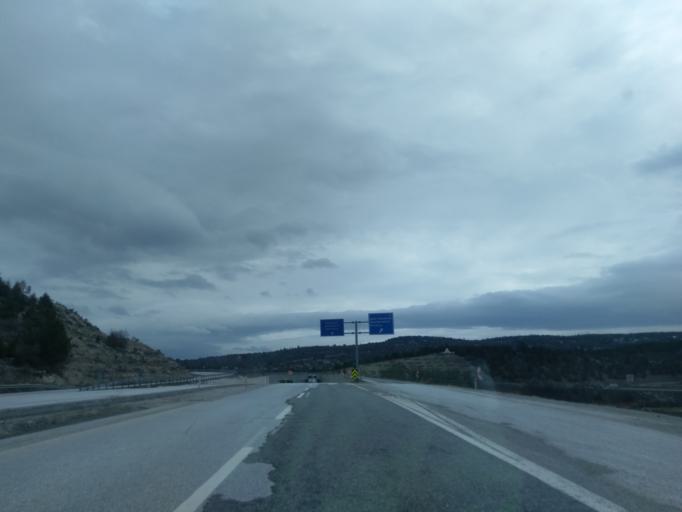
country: TR
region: Kuetahya
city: Kutahya
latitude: 39.3694
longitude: 30.0639
